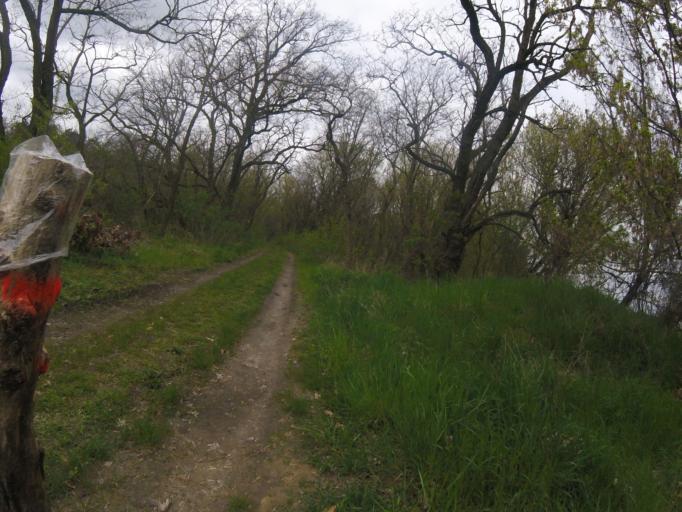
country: DE
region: Brandenburg
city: Mittenwalde
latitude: 52.2477
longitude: 13.5841
